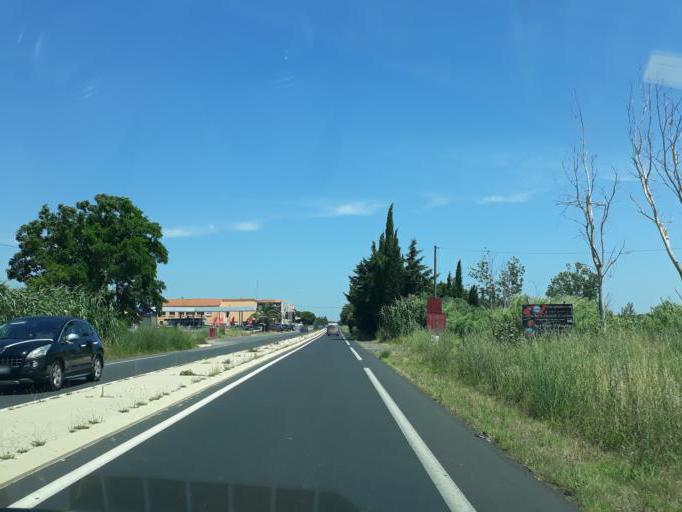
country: FR
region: Languedoc-Roussillon
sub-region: Departement de l'Herault
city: Portiragnes
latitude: 43.3135
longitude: 3.3425
